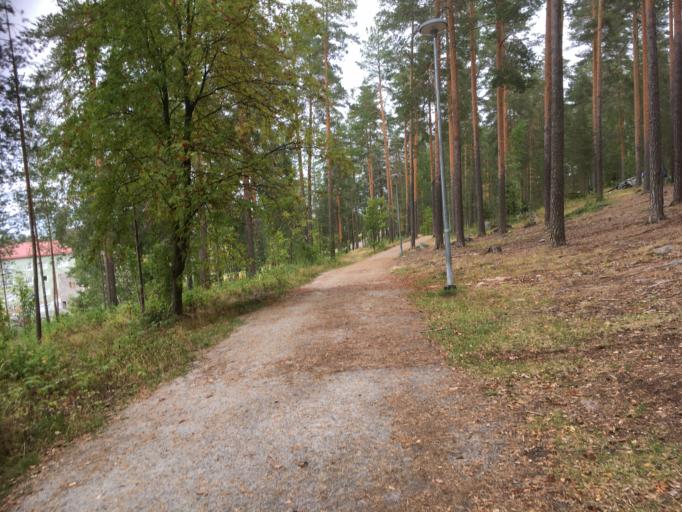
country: FI
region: Central Finland
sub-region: Jyvaeskylae
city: Jyvaeskylae
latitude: 62.2416
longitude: 25.7362
